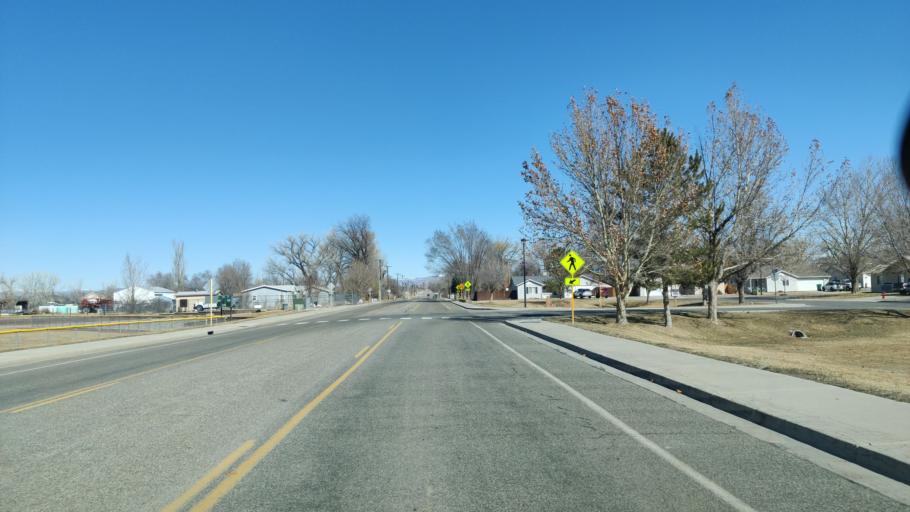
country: US
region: Colorado
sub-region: Mesa County
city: Fruita
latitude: 39.1684
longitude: -108.7197
